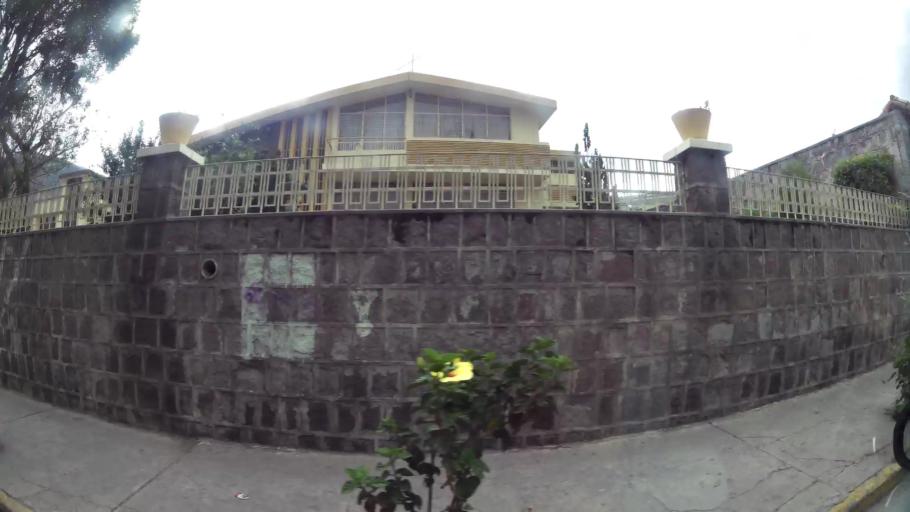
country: EC
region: Pichincha
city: Quito
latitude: -0.0116
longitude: -78.4476
